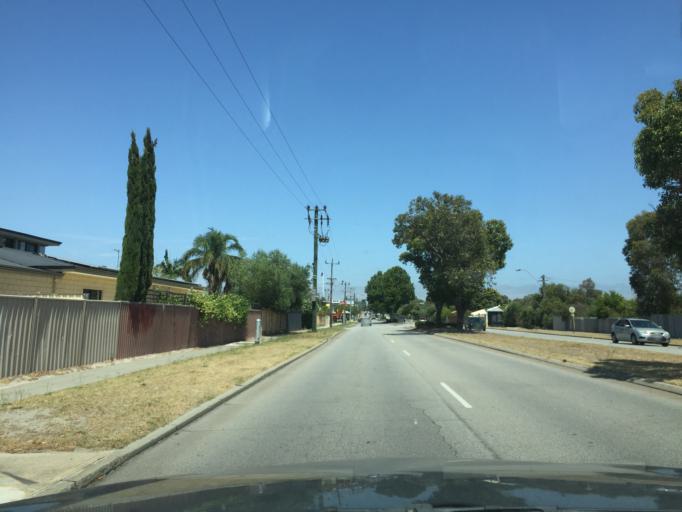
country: AU
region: Western Australia
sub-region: Canning
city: Ferndale
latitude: -32.0385
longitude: 115.9105
